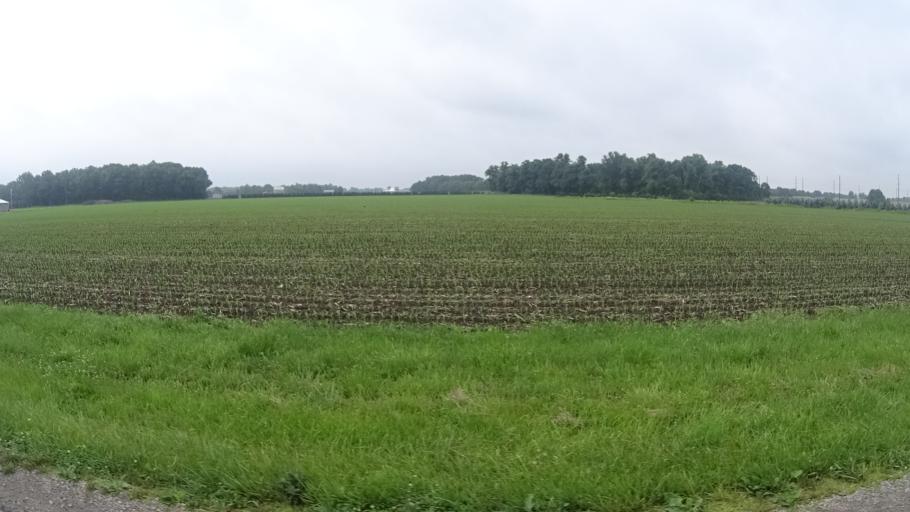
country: US
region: Ohio
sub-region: Erie County
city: Sandusky
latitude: 41.3574
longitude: -82.7400
